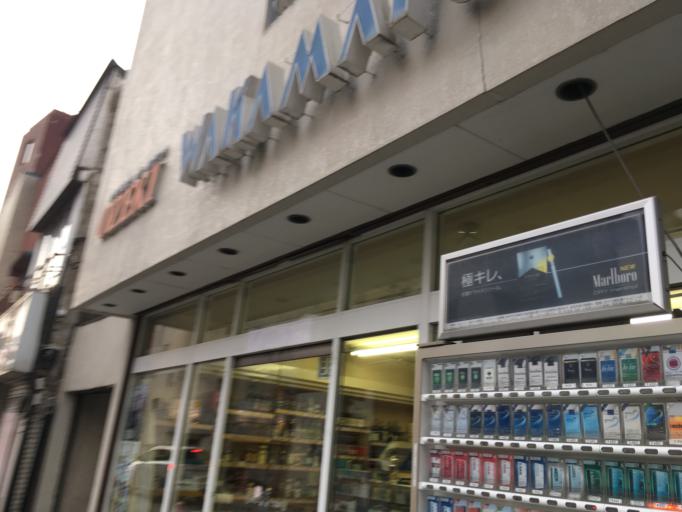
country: JP
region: Tochigi
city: Utsunomiya-shi
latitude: 36.5586
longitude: 139.8857
